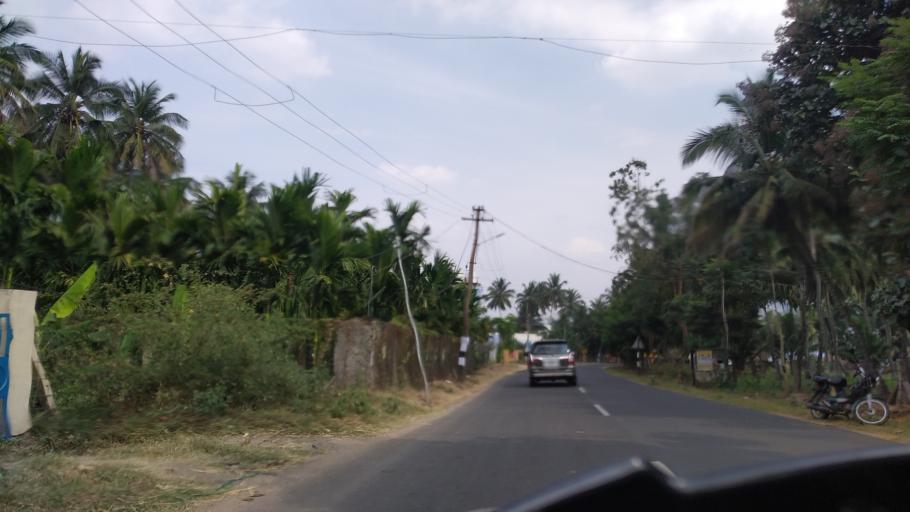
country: IN
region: Tamil Nadu
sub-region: Coimbatore
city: Perur
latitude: 10.9537
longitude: 76.7621
